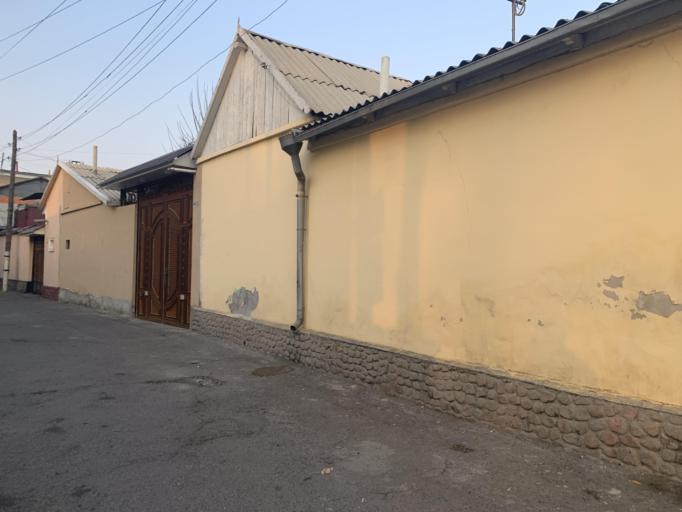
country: UZ
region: Fergana
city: Qo`qon
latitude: 40.5300
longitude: 70.9328
